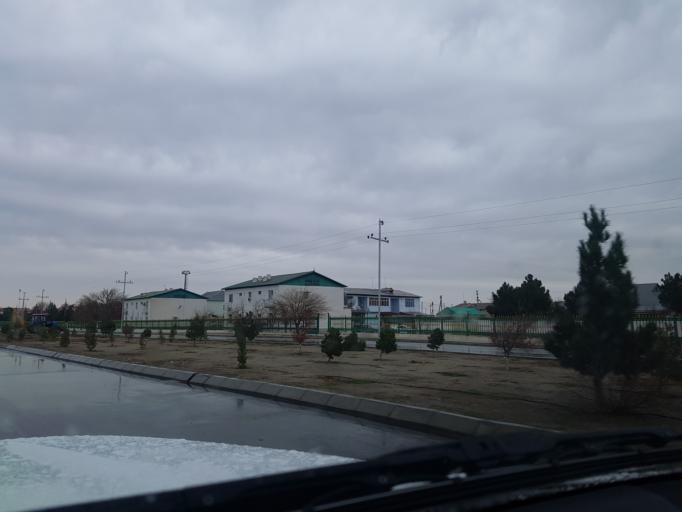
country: TM
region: Balkan
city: Balkanabat
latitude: 39.5095
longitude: 54.3470
